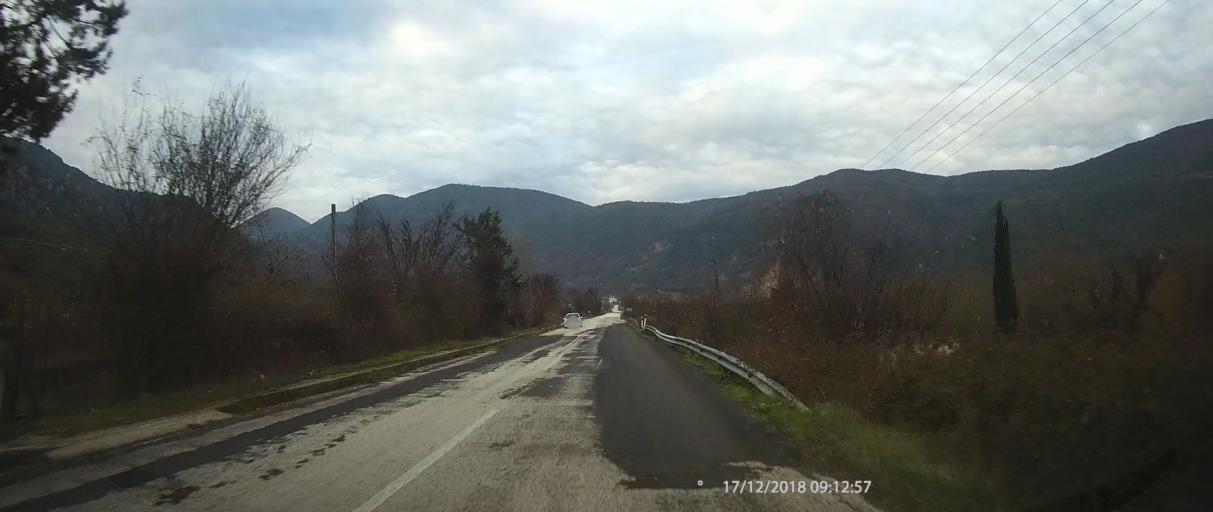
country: GR
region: Epirus
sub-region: Nomos Ioanninon
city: Kalpaki
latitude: 39.9768
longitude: 20.6630
